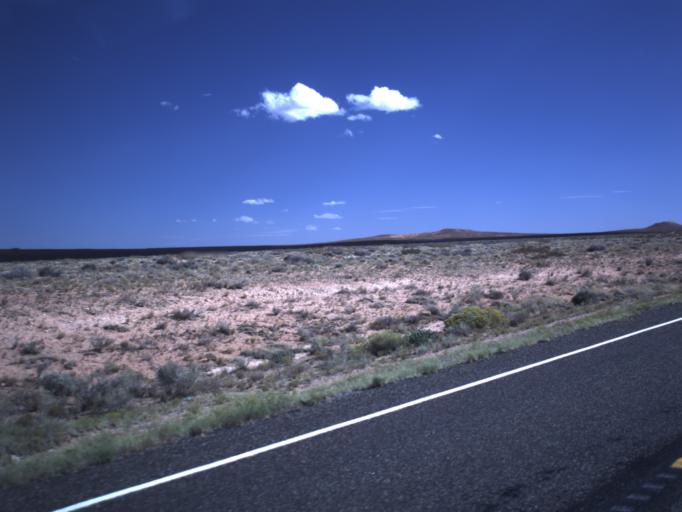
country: US
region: Utah
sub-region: Wayne County
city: Loa
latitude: 38.1740
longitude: -110.6247
